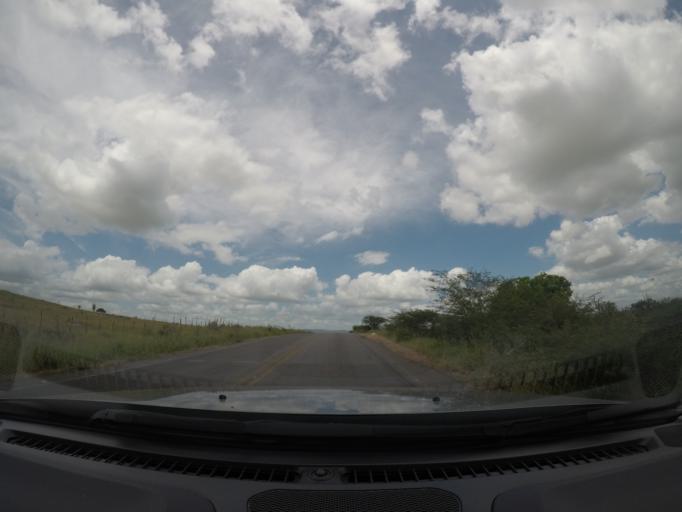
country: BR
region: Bahia
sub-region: Ipira
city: Ipira
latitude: -12.2526
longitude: -39.8154
